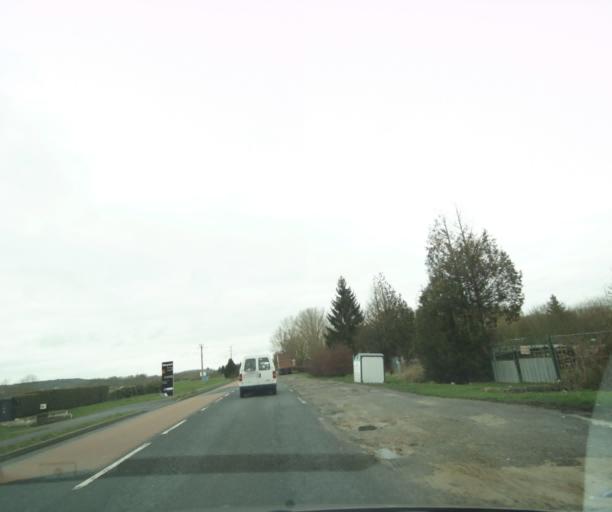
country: FR
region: Picardie
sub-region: Departement de l'Oise
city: Noyon
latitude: 49.5874
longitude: 2.9907
